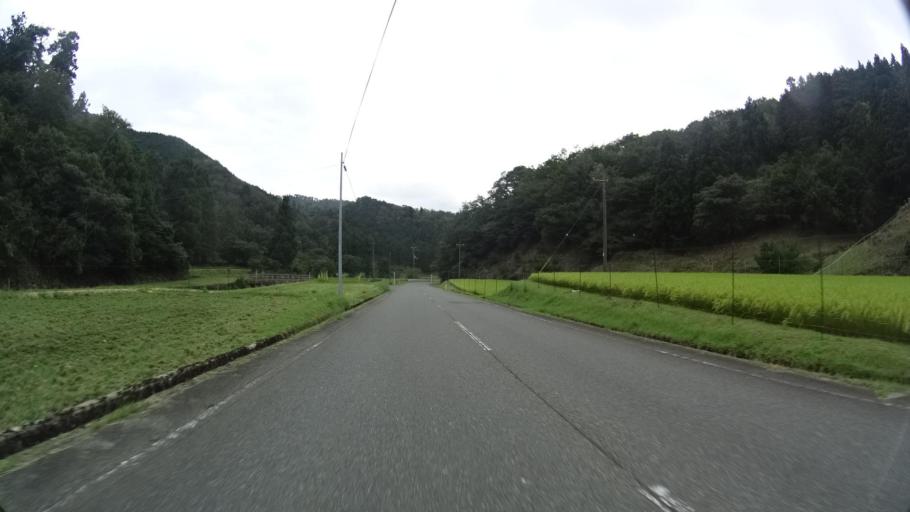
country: JP
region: Kyoto
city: Miyazu
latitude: 35.4650
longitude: 135.1534
